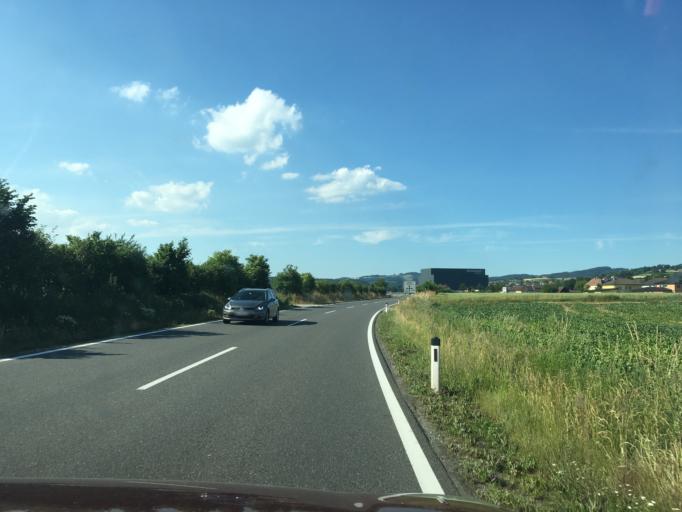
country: AT
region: Upper Austria
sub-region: Politischer Bezirk Perg
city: Perg
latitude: 48.2549
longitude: 14.5776
